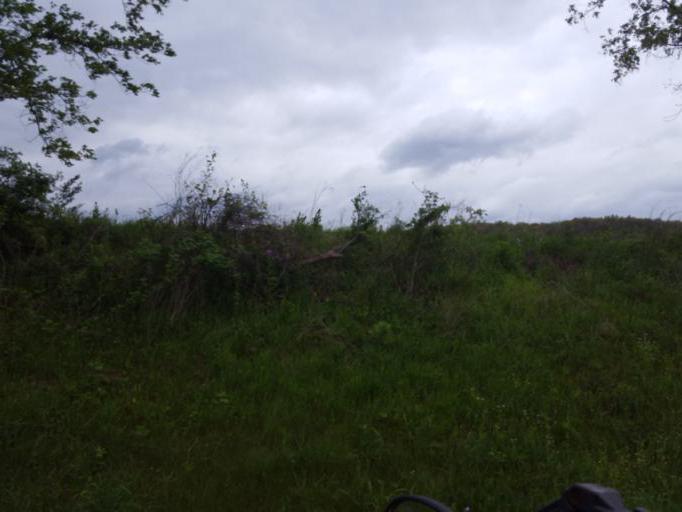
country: US
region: Ohio
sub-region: Ashland County
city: Loudonville
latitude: 40.5678
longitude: -82.1911
